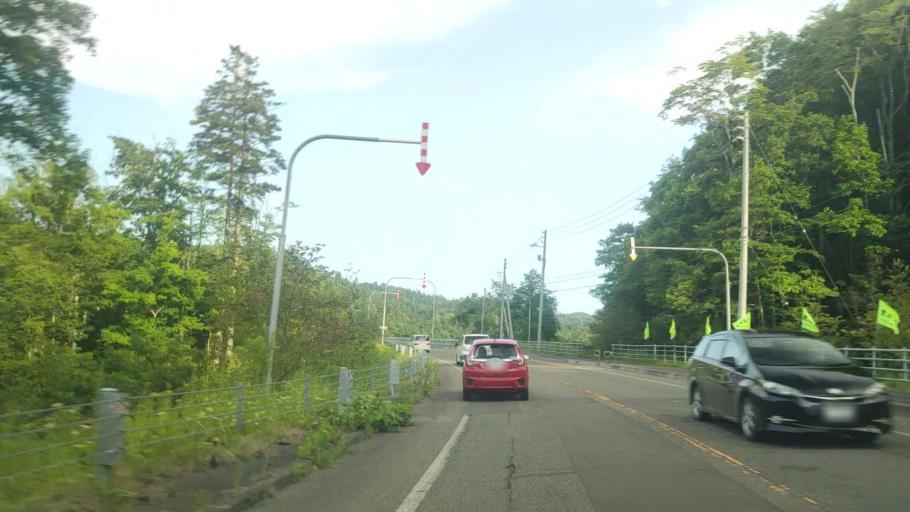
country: JP
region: Hokkaido
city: Iwamizawa
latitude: 43.0220
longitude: 141.9456
